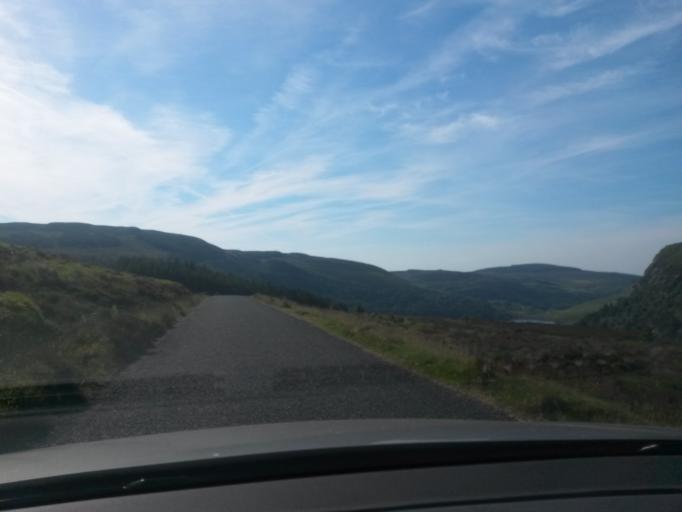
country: IE
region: Leinster
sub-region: Wicklow
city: Enniskerry
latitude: 53.1209
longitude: -6.2744
